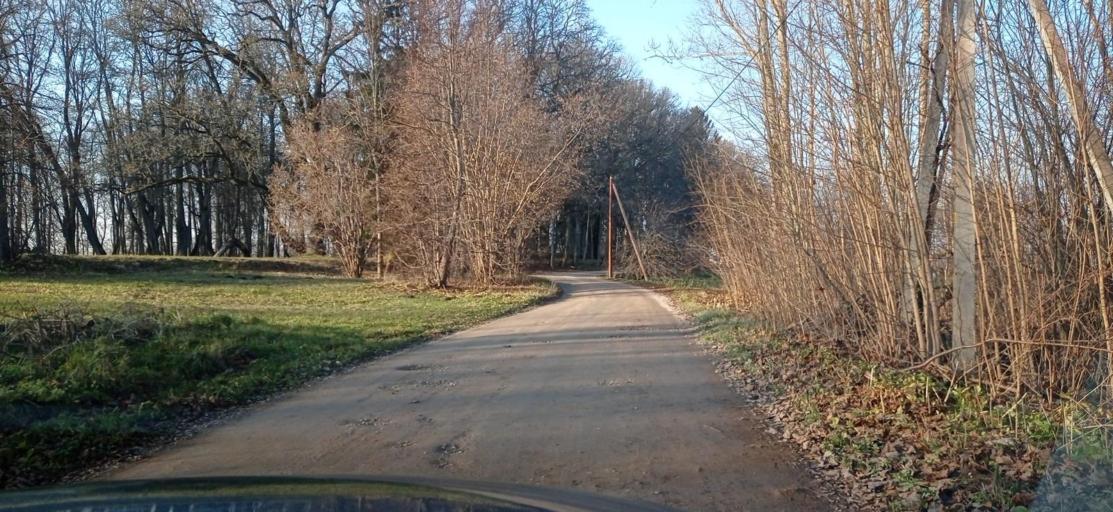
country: EE
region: Jogevamaa
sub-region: Tabivere vald
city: Tabivere
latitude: 58.6718
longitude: 26.7611
